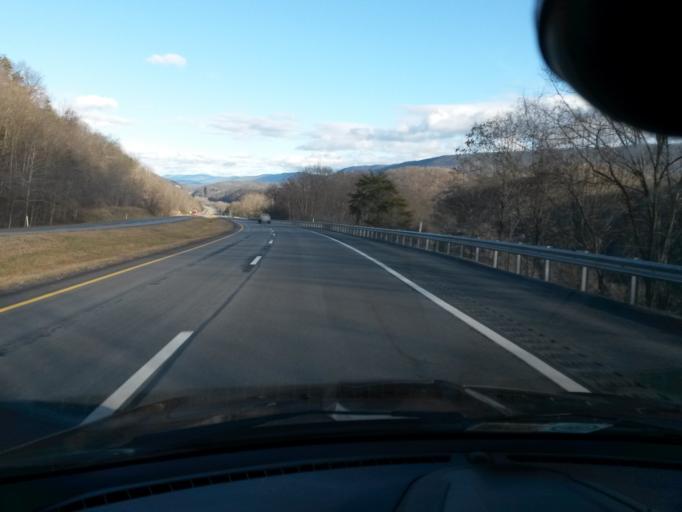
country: US
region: West Virginia
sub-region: Mercer County
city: Athens
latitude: 37.3445
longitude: -80.9353
